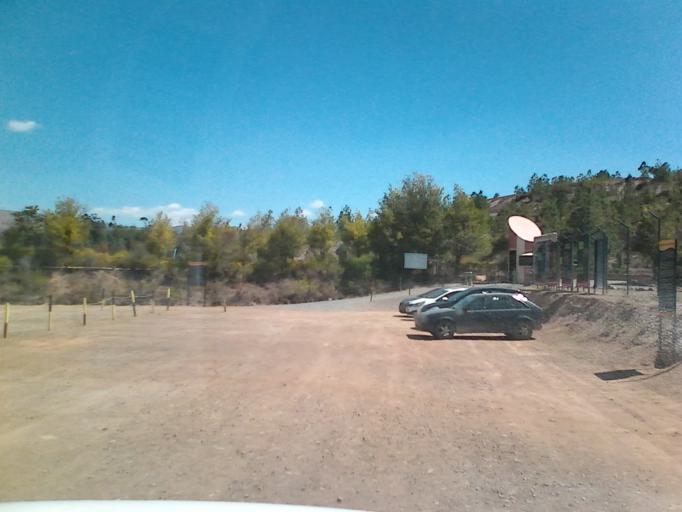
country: CO
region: Boyaca
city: Villa de Leiva
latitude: 5.6299
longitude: -73.5705
